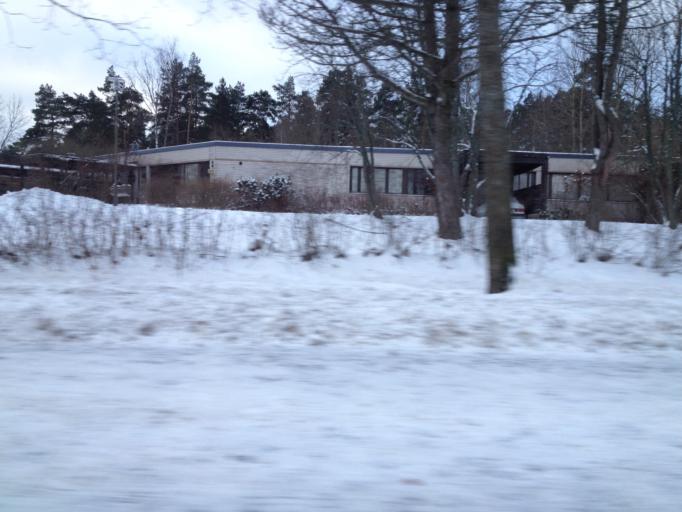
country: FI
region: Uusimaa
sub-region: Helsinki
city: Vantaa
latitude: 60.2132
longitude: 25.1483
